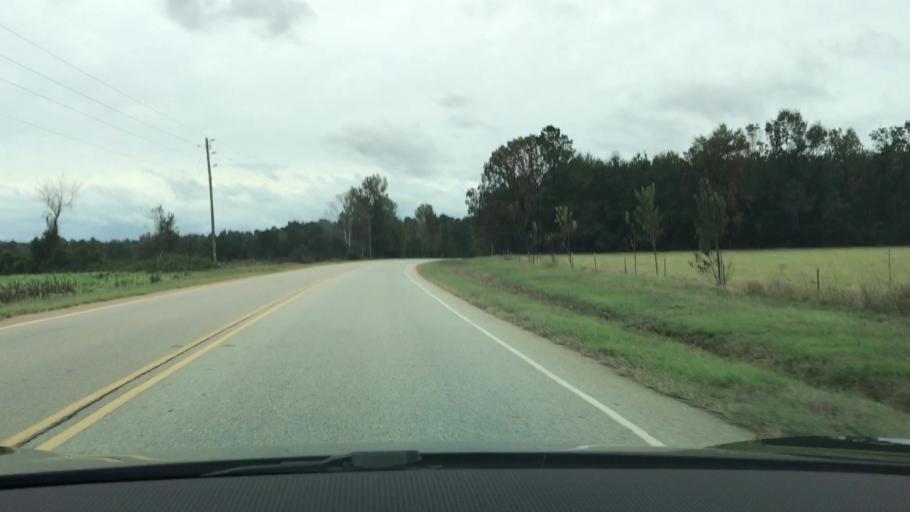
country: US
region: Georgia
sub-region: Jefferson County
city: Louisville
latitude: 33.0984
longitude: -82.4204
